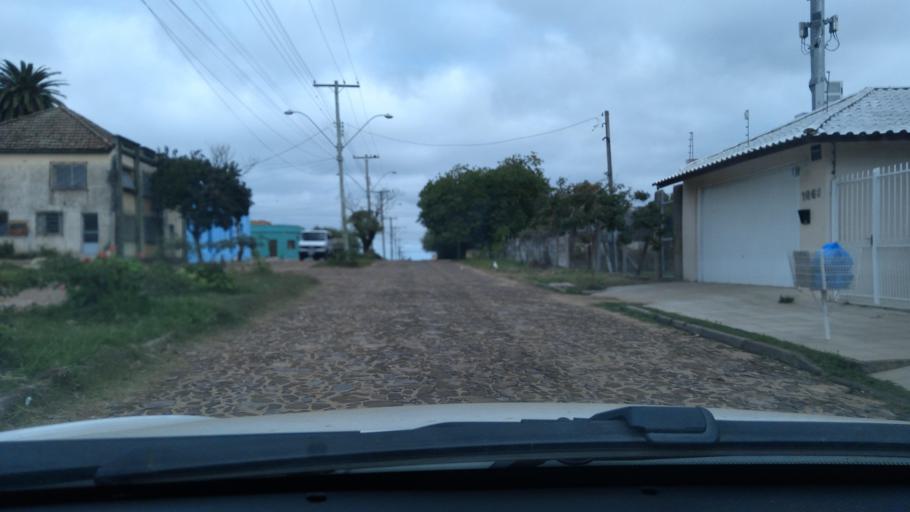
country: BR
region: Rio Grande do Sul
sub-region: Dom Pedrito
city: Dom Pedrito
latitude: -30.9860
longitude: -54.6635
